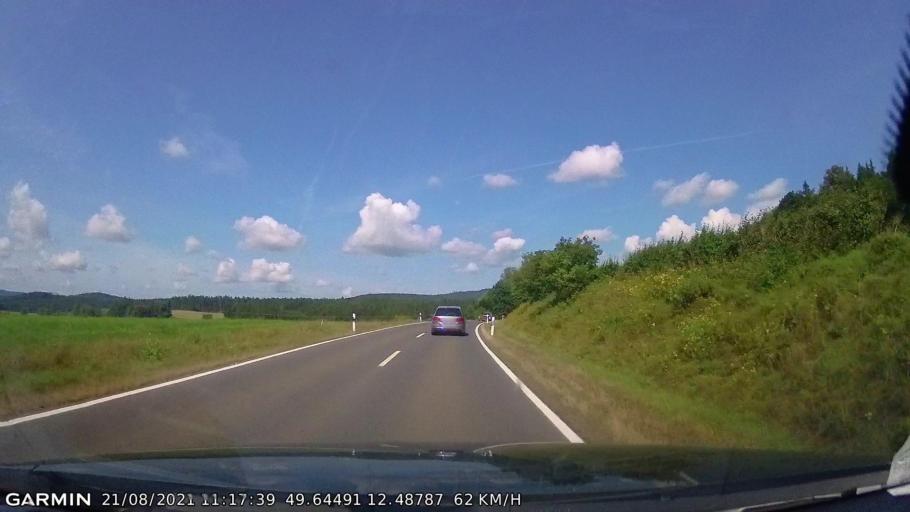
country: DE
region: Bavaria
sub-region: Upper Palatinate
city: Waidhaus
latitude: 49.6449
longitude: 12.4879
